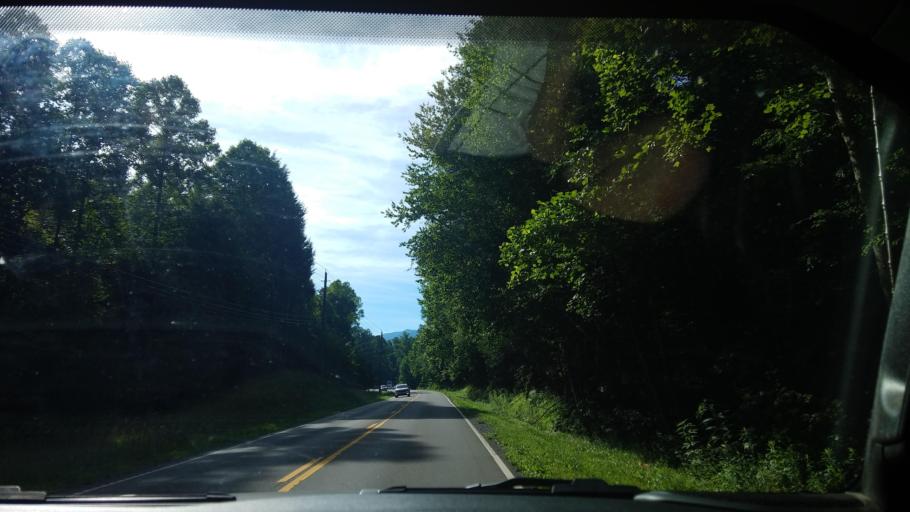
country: US
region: Tennessee
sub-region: Sevier County
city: Gatlinburg
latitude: 35.7586
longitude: -83.3646
